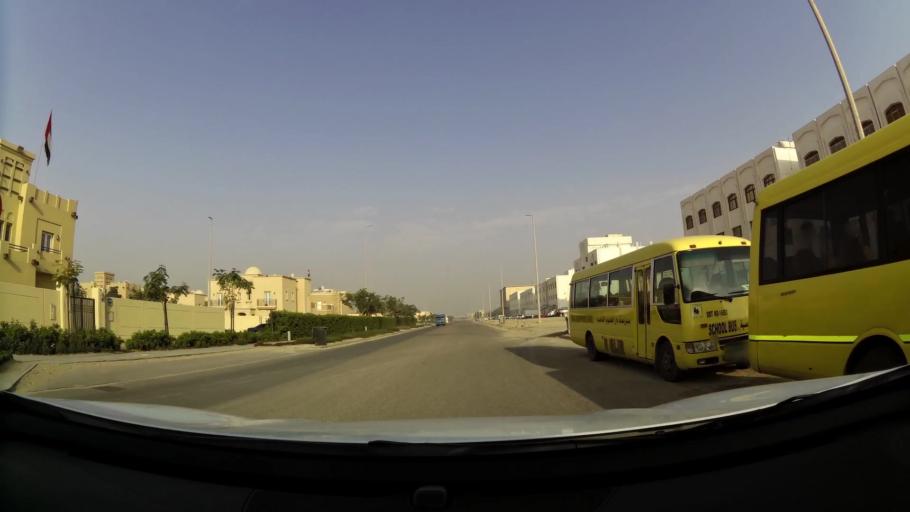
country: AE
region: Abu Dhabi
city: Abu Dhabi
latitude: 24.3003
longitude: 54.6185
